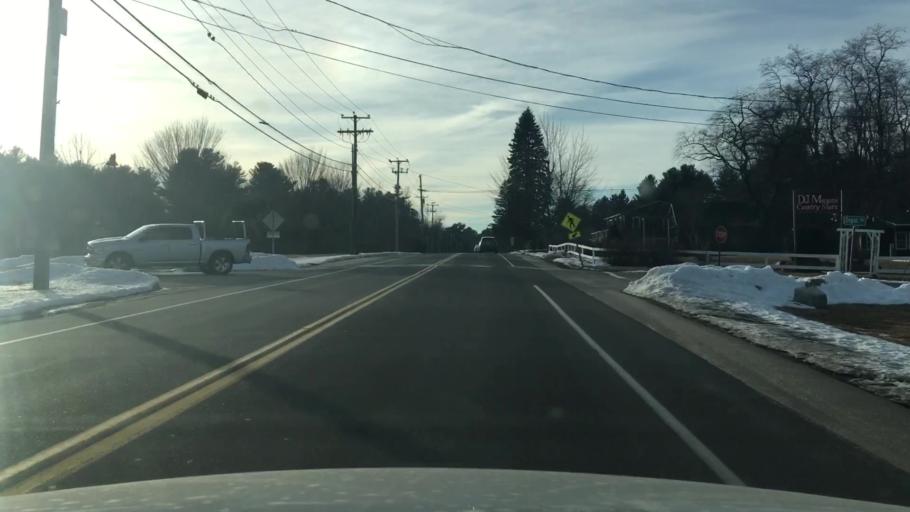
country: US
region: Maine
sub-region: York County
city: Wells Beach Station
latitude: 43.3215
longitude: -70.5936
